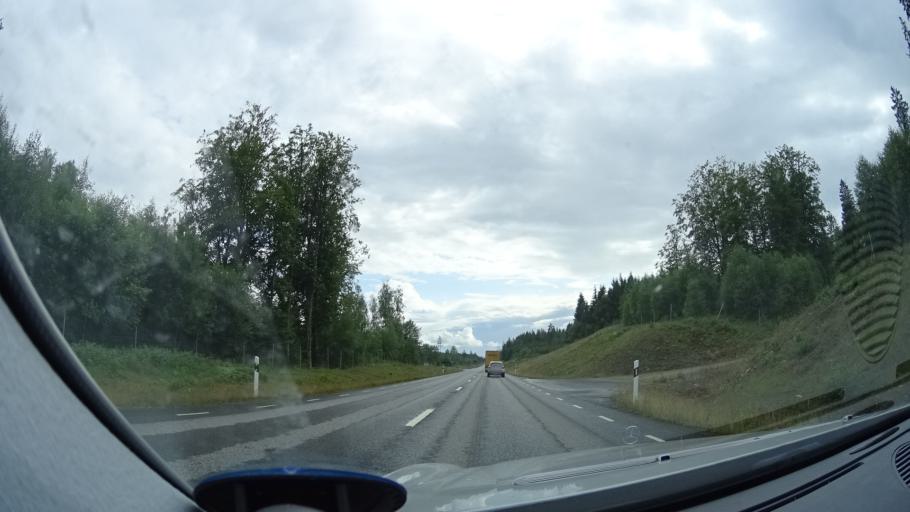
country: SE
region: Blekinge
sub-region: Karlshamns Kommun
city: Svangsta
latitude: 56.2946
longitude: 14.8793
